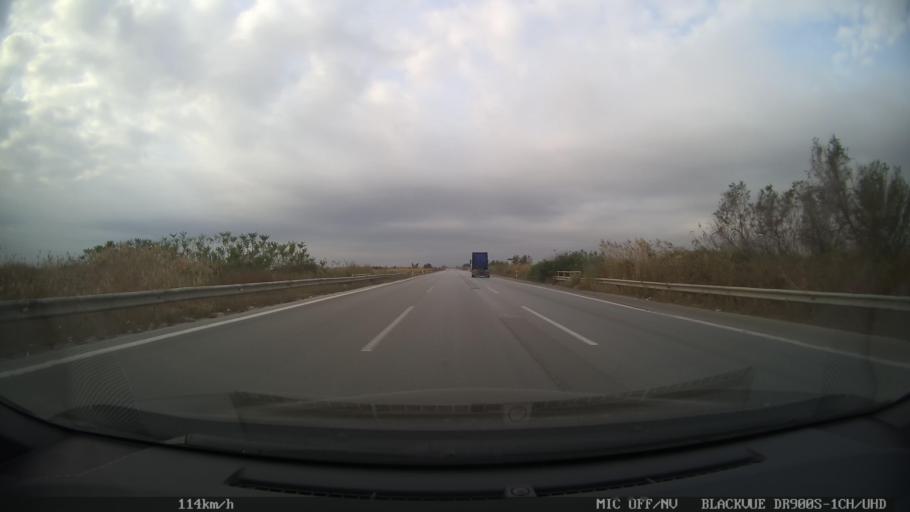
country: GR
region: Central Macedonia
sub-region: Nomos Thessalonikis
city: Chalastra
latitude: 40.6278
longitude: 22.7694
